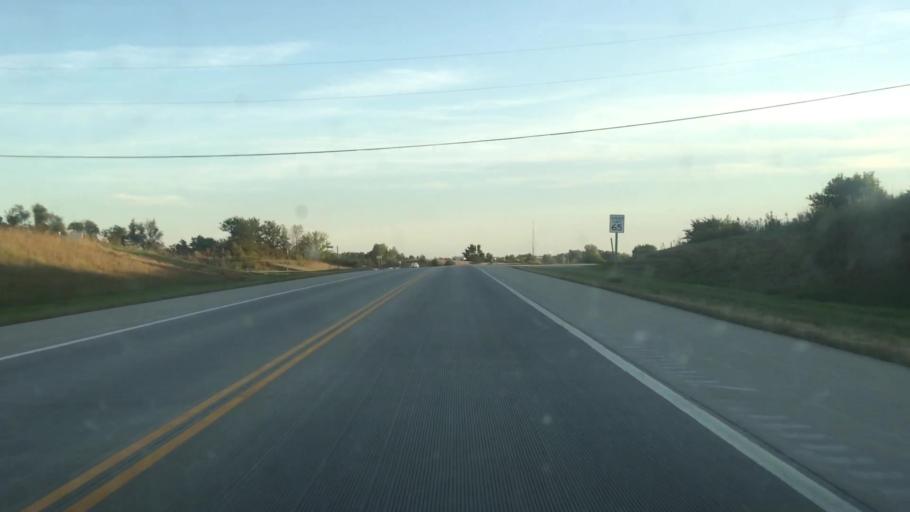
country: US
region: Kansas
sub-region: Leavenworth County
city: Leavenworth
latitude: 39.3808
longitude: -95.0575
